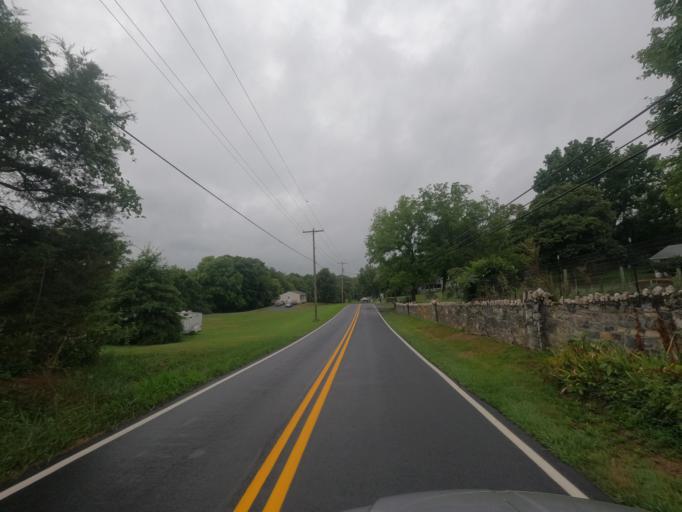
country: US
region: Maryland
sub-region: Washington County
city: Wilson-Conococheague
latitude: 39.6266
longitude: -77.9433
